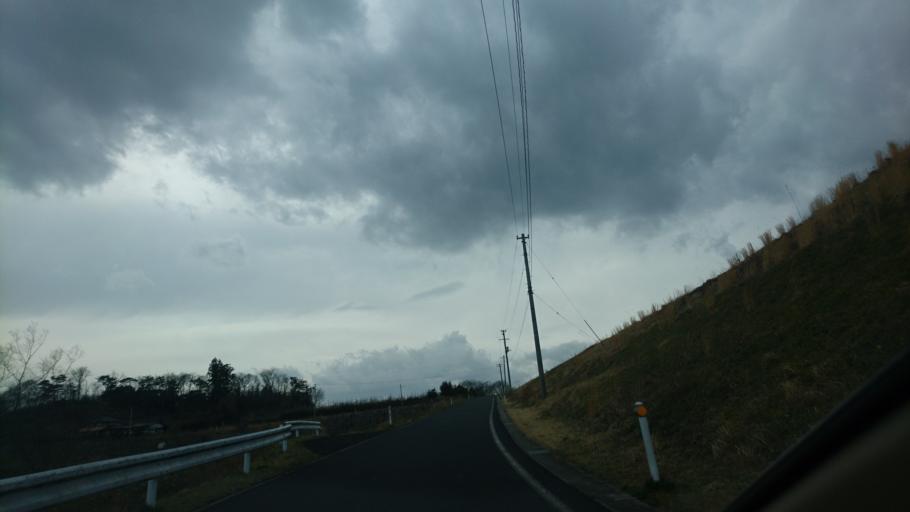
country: JP
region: Iwate
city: Ichinoseki
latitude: 38.8829
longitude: 141.1642
